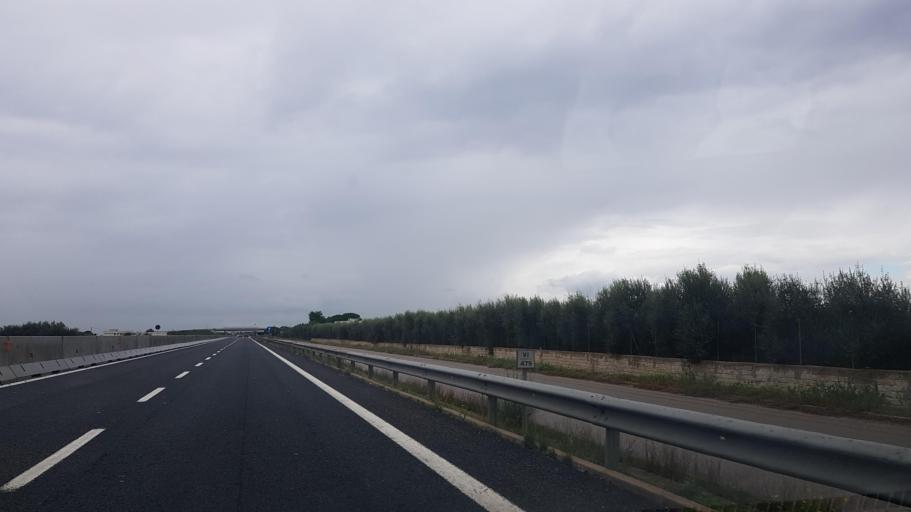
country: IT
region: Apulia
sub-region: Provincia di Taranto
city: Massafra
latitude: 40.5308
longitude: 17.0924
